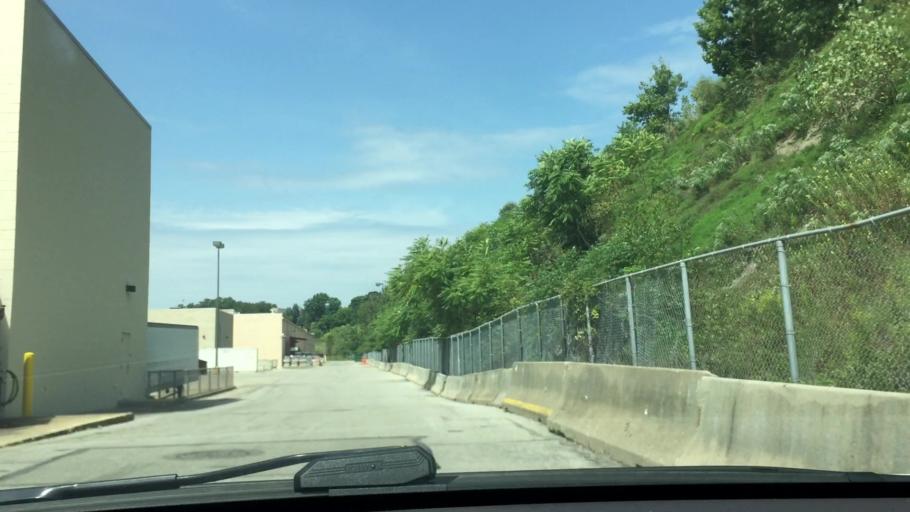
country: US
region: Pennsylvania
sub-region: Allegheny County
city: Pleasant Hills
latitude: 40.3406
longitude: -79.9499
